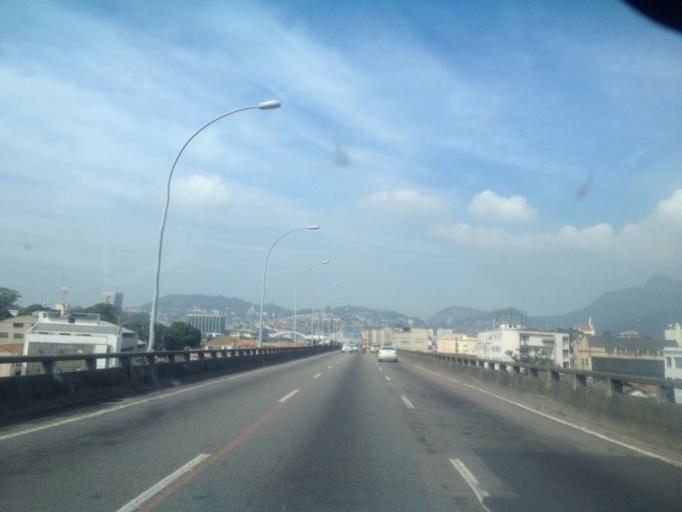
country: BR
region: Rio de Janeiro
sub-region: Rio De Janeiro
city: Rio de Janeiro
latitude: -22.9001
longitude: -43.2177
